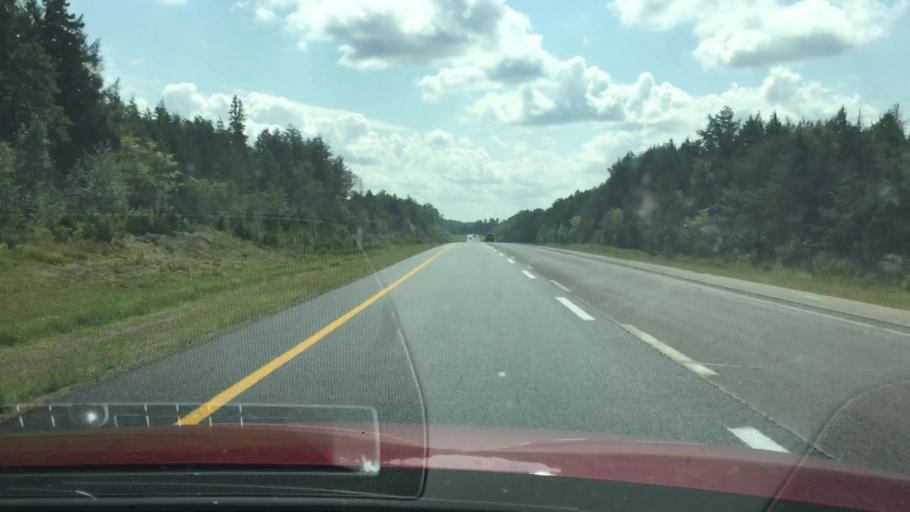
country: US
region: Maine
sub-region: Penobscot County
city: Medway
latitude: 45.7300
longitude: -68.4727
